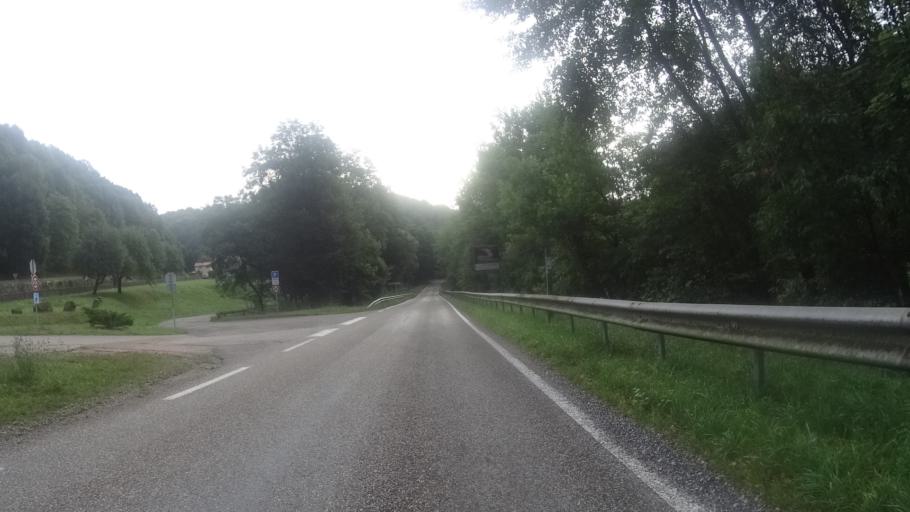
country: FR
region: Lorraine
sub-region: Departement de la Moselle
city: Niderviller
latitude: 48.7243
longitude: 7.1821
